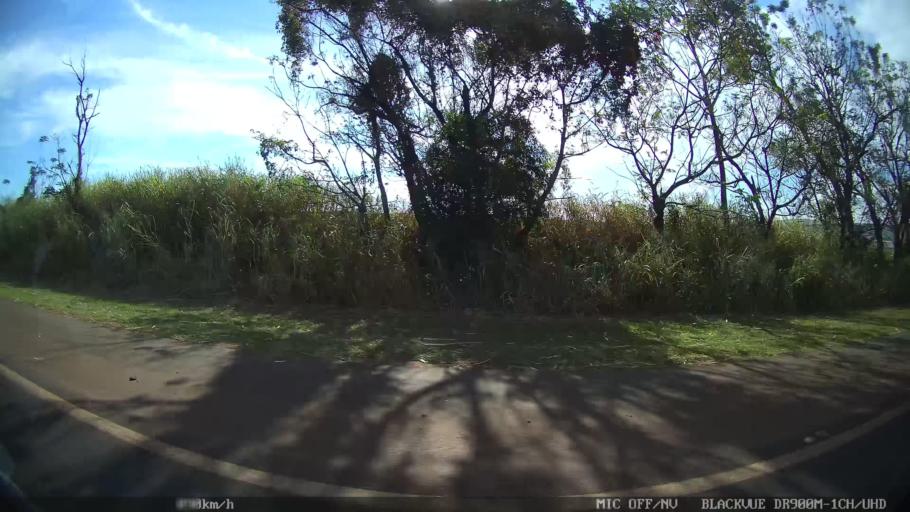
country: BR
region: Sao Paulo
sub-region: Americo Brasiliense
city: Americo Brasiliense
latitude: -21.7619
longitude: -48.0786
